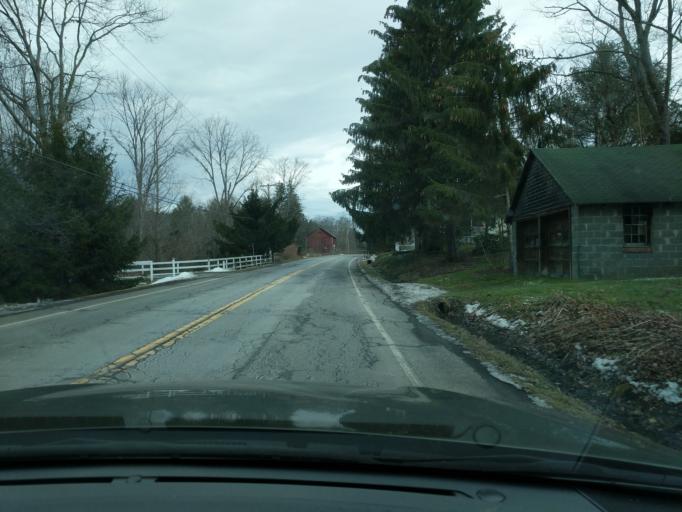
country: US
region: New York
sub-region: Tompkins County
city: East Ithaca
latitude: 42.3821
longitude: -76.3856
